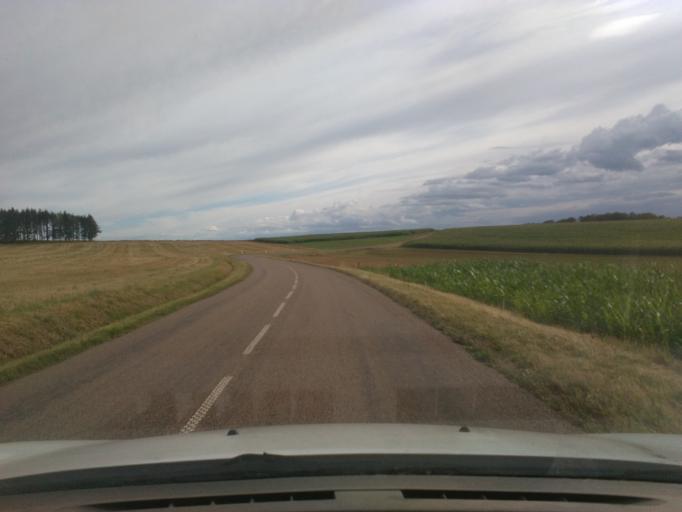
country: FR
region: Lorraine
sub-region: Departement des Vosges
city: Chatel-sur-Moselle
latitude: 48.3363
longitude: 6.4207
